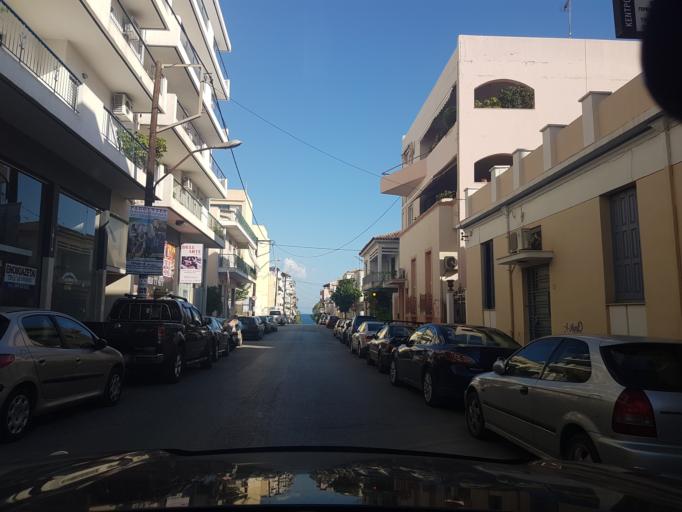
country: GR
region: Central Greece
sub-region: Nomos Evvoias
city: Chalkida
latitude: 38.4688
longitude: 23.6005
